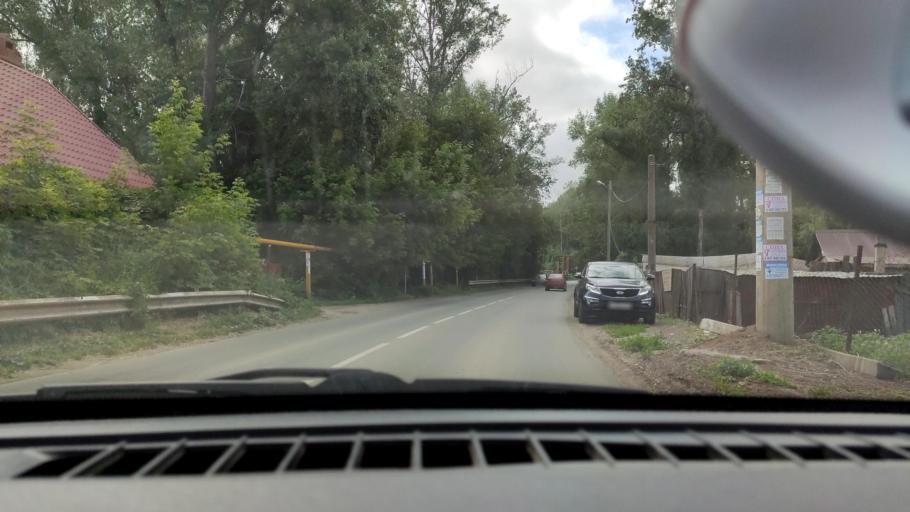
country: RU
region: Samara
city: Novokuybyshevsk
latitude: 53.1513
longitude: 49.9802
